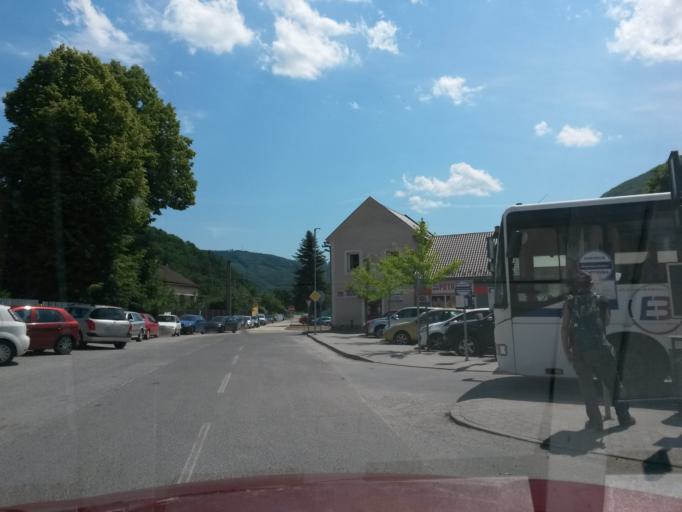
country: SK
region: Kosicky
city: Gelnica
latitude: 48.8940
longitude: 21.0138
